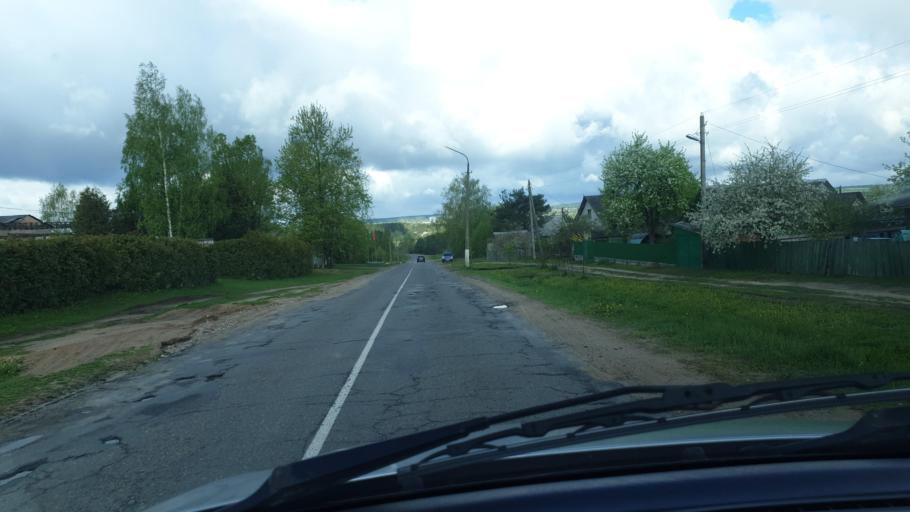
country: BY
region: Vitebsk
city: Lyepyel'
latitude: 54.8755
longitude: 28.6770
